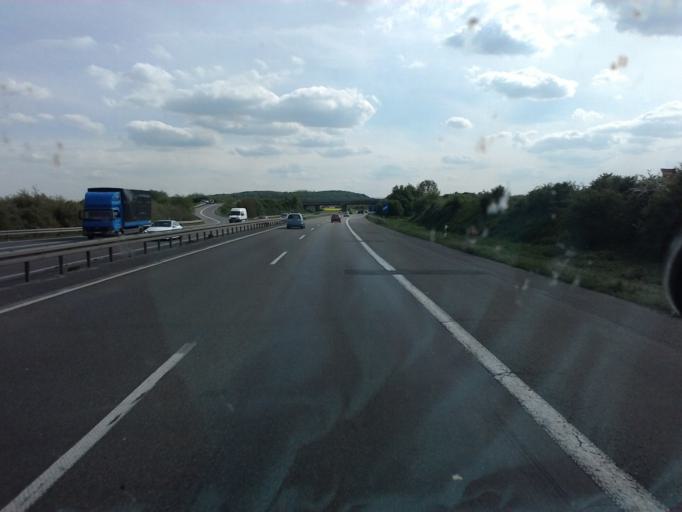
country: DE
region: North Rhine-Westphalia
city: Rheinberg
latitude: 51.5159
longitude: 6.5855
